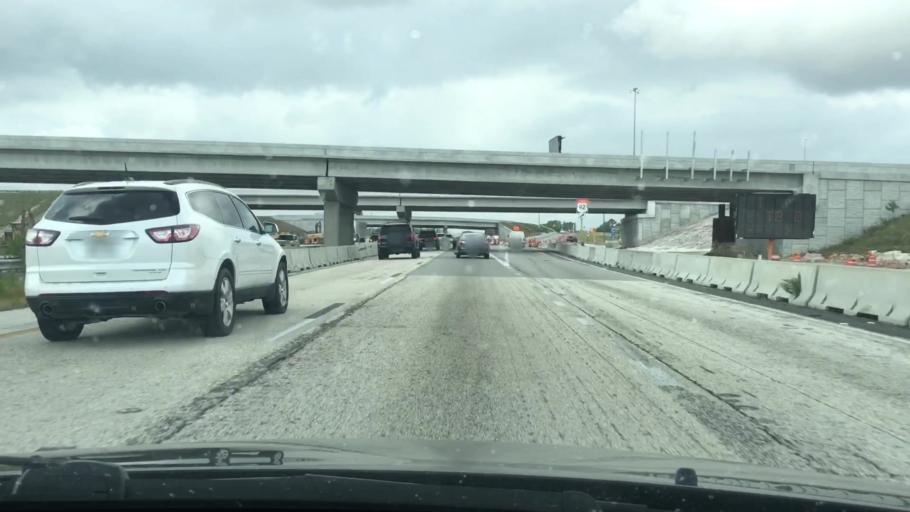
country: US
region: Florida
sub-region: Volusia County
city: South Daytona
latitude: 29.1546
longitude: -81.0751
